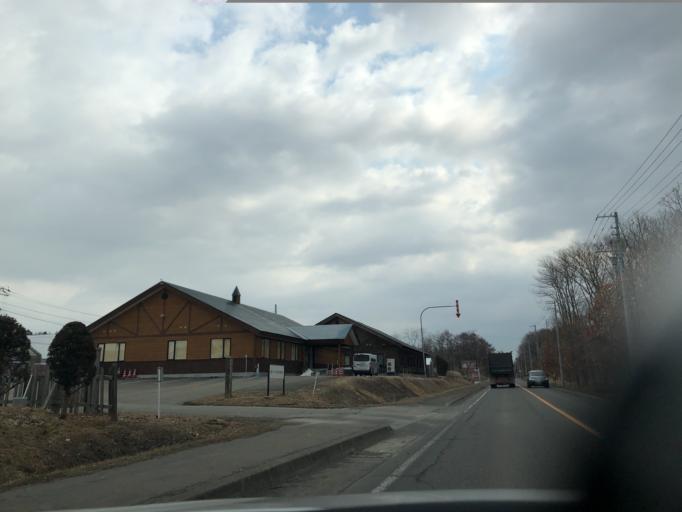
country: JP
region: Hokkaido
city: Chitose
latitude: 42.7603
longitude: 141.7827
